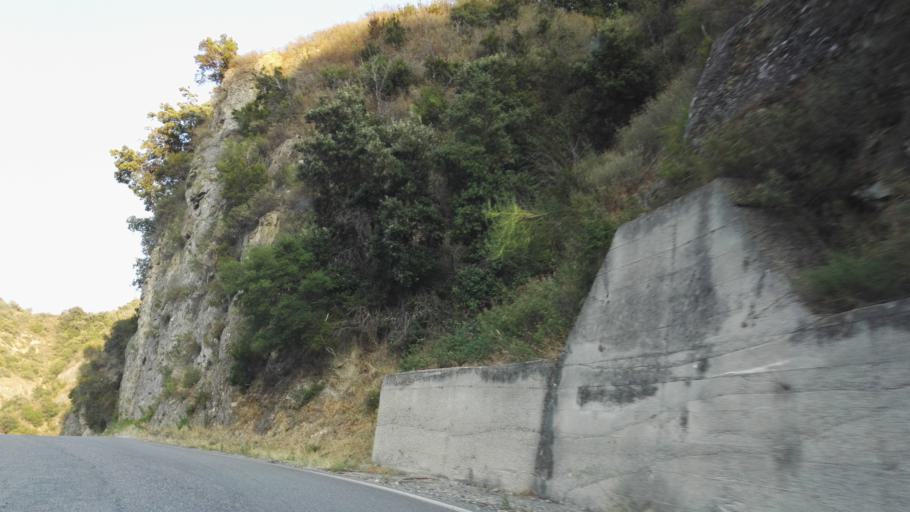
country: IT
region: Calabria
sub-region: Provincia di Reggio Calabria
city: Caulonia
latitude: 38.4004
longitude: 16.4122
